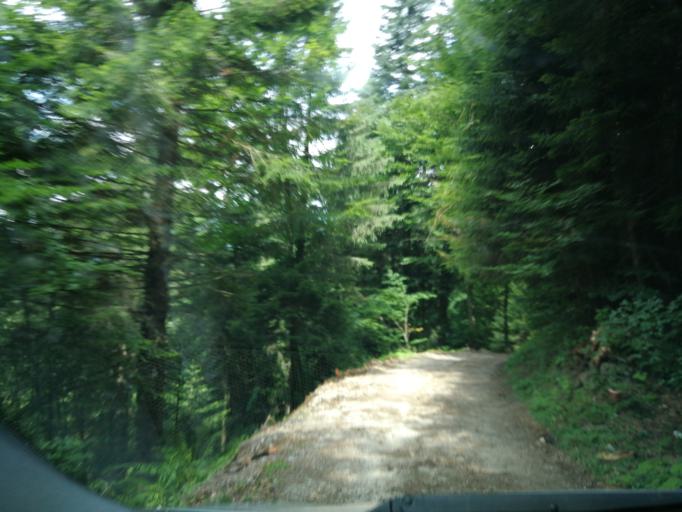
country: IT
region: Trentino-Alto Adige
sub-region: Provincia di Trento
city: Castel Condino
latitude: 45.9297
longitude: 10.6082
